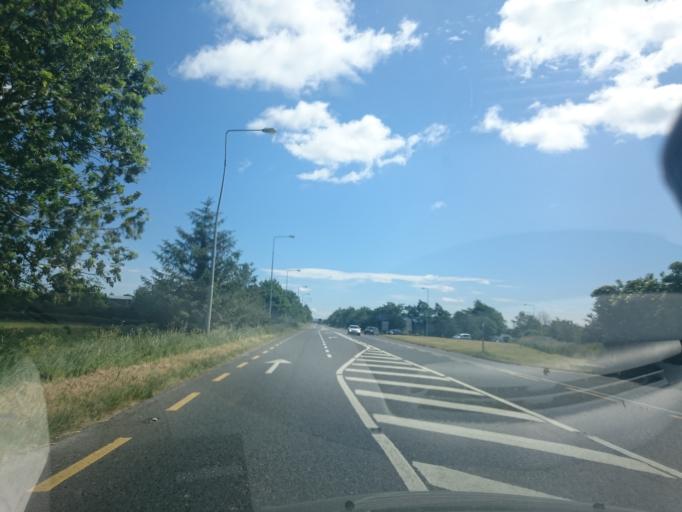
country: IE
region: Leinster
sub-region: Kilkenny
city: Thomastown
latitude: 52.6471
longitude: -7.1276
